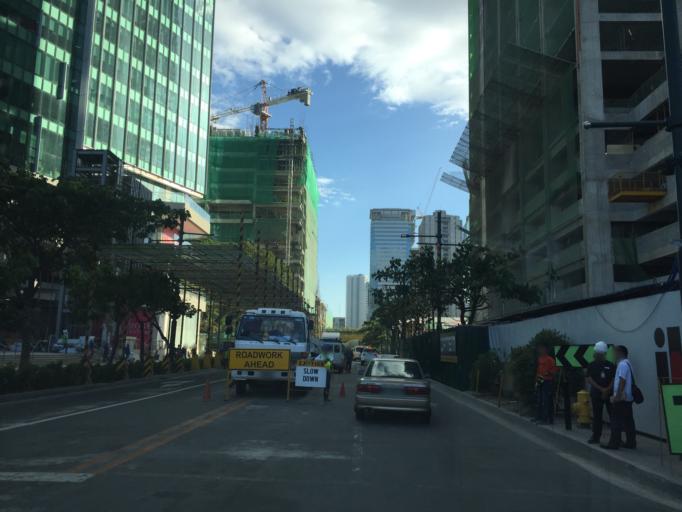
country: PH
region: Metro Manila
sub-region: Makati City
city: Makati City
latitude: 14.5573
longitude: 121.0535
